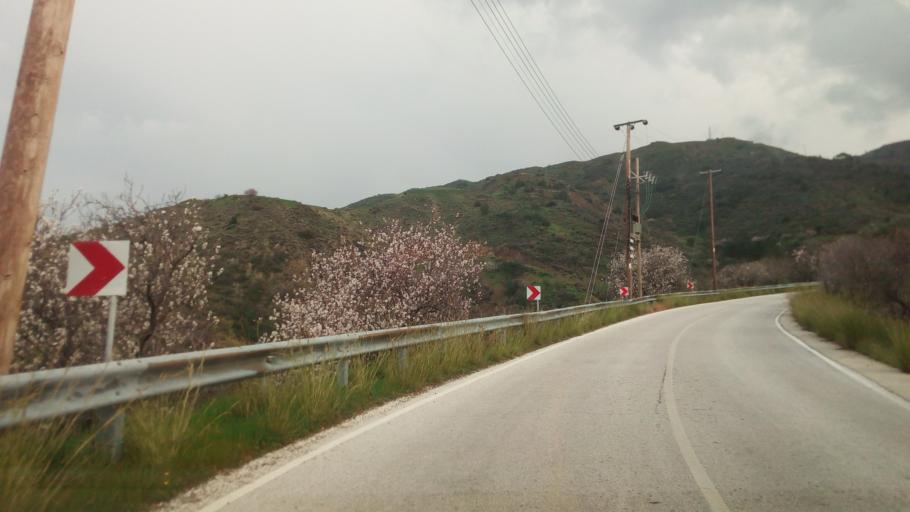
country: CY
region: Lefkosia
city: Kato Pyrgos
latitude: 35.1712
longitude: 32.5904
